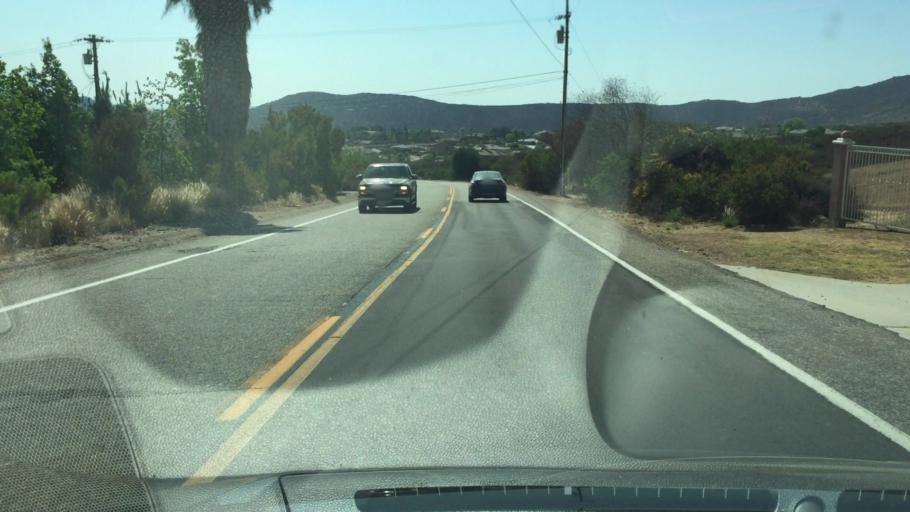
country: US
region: California
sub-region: San Diego County
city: Jamul
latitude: 32.7356
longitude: -116.8435
